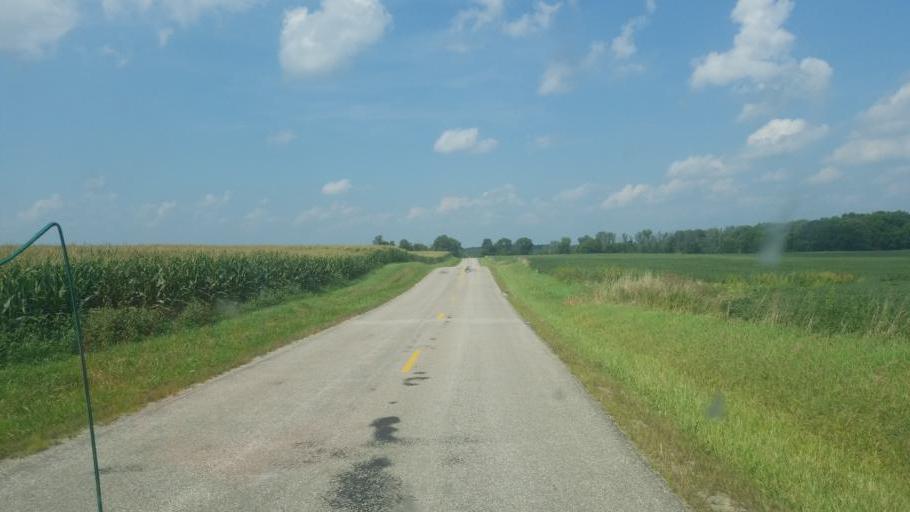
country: US
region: Ohio
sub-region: Huron County
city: New London
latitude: 41.0573
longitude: -82.3579
